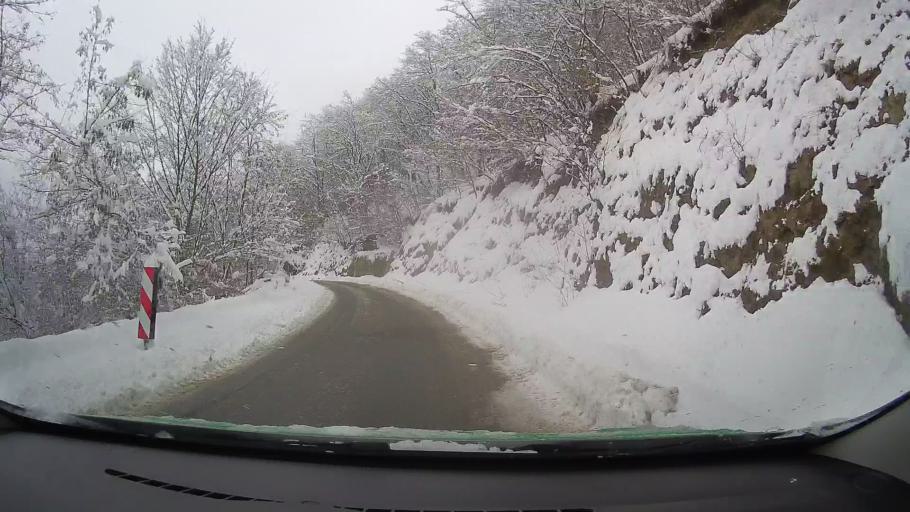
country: RO
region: Alba
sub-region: Comuna Sugag
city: Dobra
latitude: 45.7584
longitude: 23.6641
